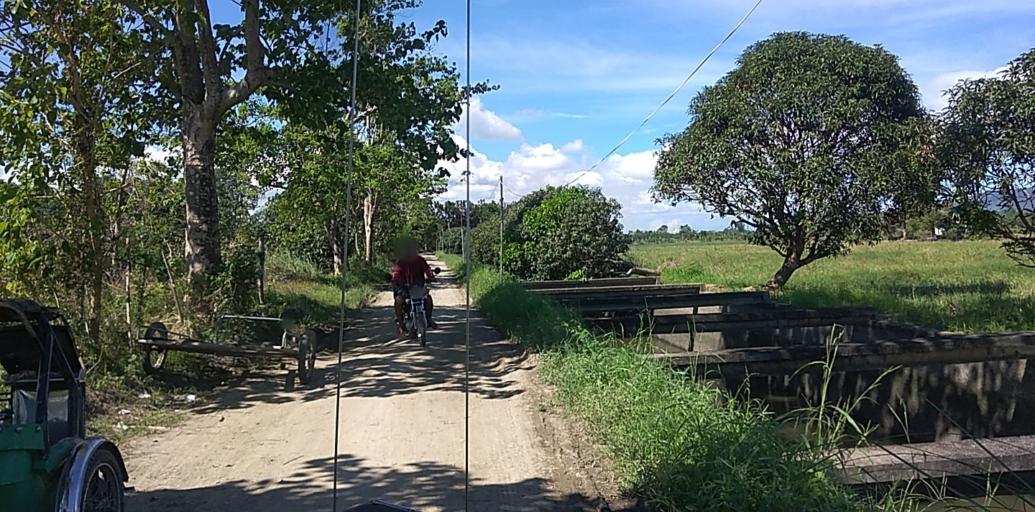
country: PH
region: Central Luzon
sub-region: Province of Pampanga
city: Arayat
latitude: 15.1285
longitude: 120.7912
